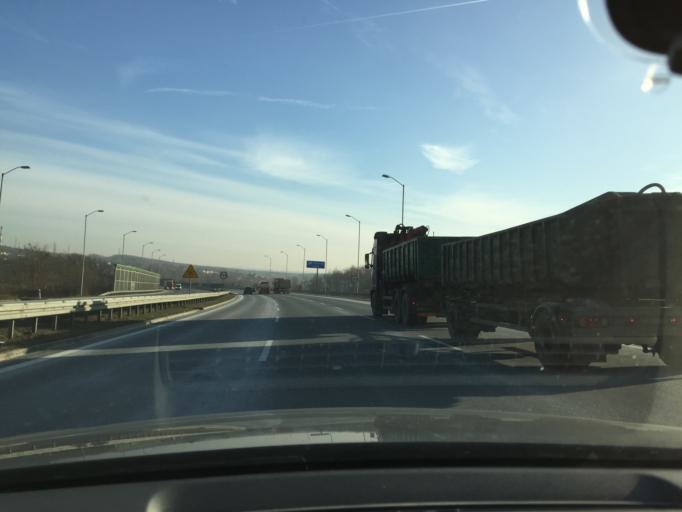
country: PL
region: Silesian Voivodeship
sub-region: Ruda Slaska
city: Ruda Slaska
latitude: 50.2489
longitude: 18.8884
